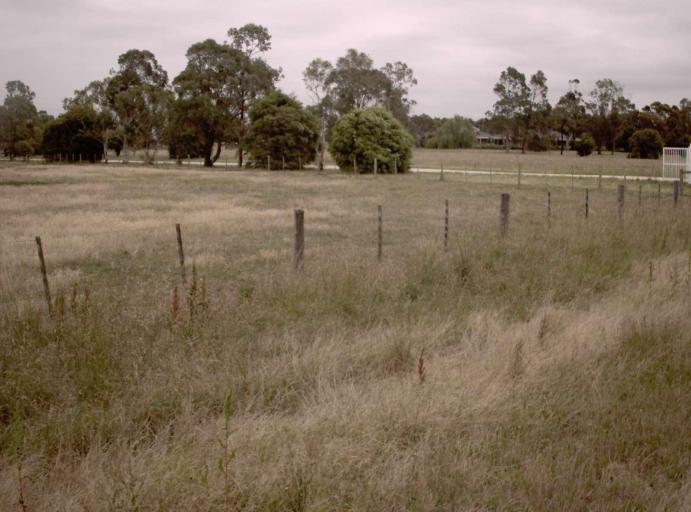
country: AU
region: Victoria
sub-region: Wellington
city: Heyfield
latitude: -38.0780
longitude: 146.7710
